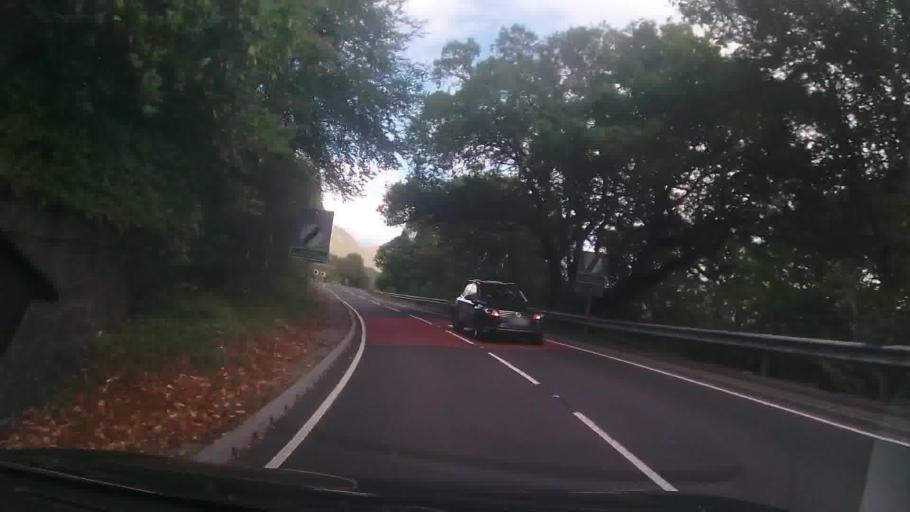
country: GB
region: Scotland
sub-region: Argyll and Bute
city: Garelochhead
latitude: 56.4048
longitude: -5.0376
